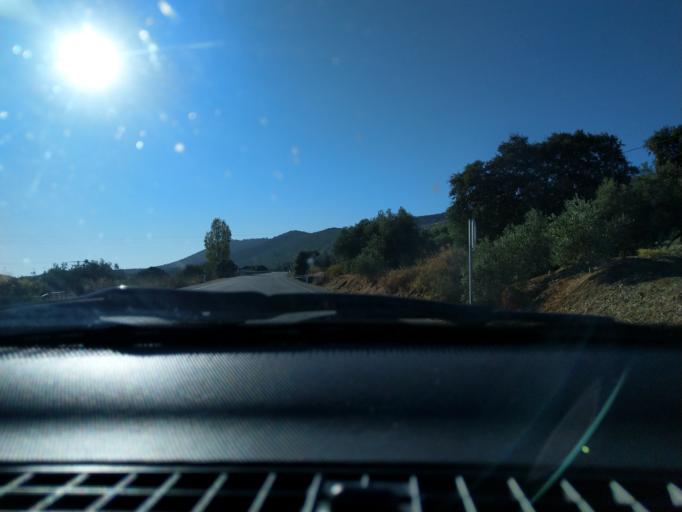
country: ES
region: Extremadura
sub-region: Provincia de Badajoz
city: Reina
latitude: 38.1438
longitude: -5.8851
